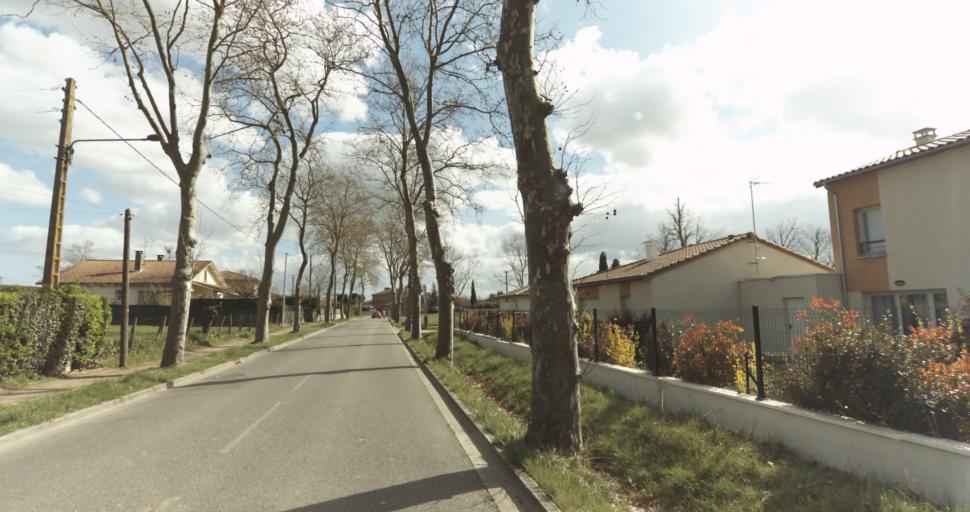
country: FR
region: Midi-Pyrenees
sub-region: Departement de la Haute-Garonne
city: Auterive
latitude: 43.3567
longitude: 1.4775
